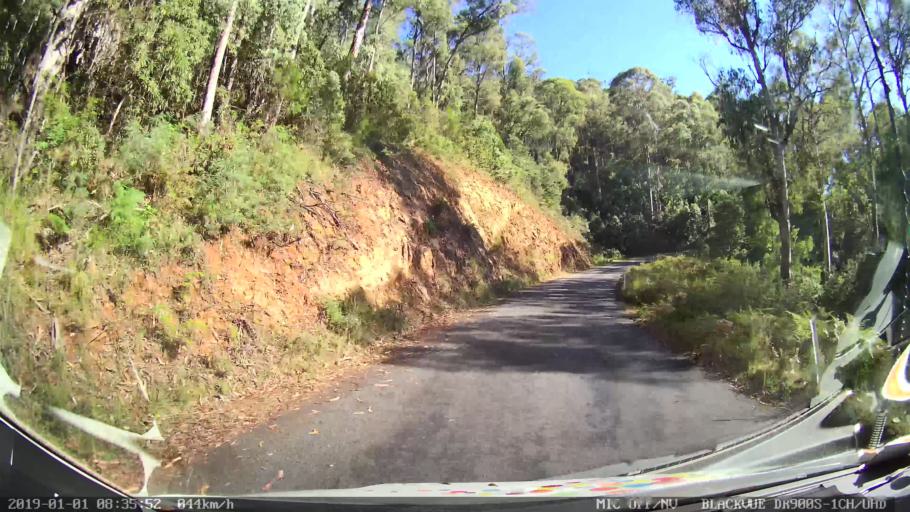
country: AU
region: New South Wales
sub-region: Snowy River
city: Jindabyne
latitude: -36.3468
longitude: 148.1934
